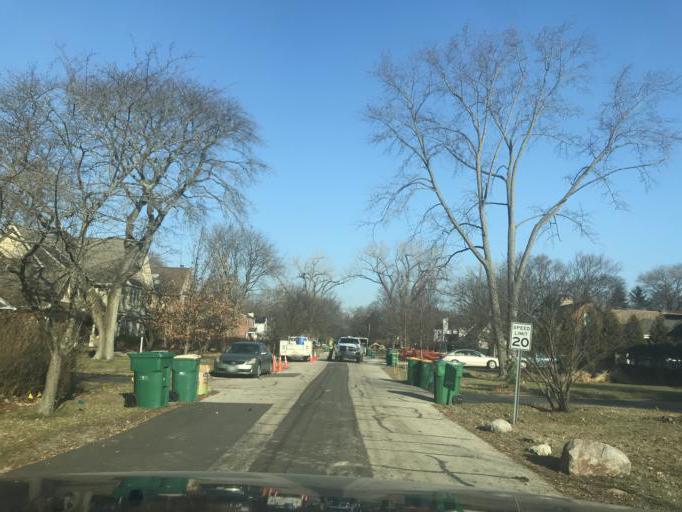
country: US
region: Illinois
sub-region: Cook County
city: Northfield
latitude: 42.0978
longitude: -87.7625
